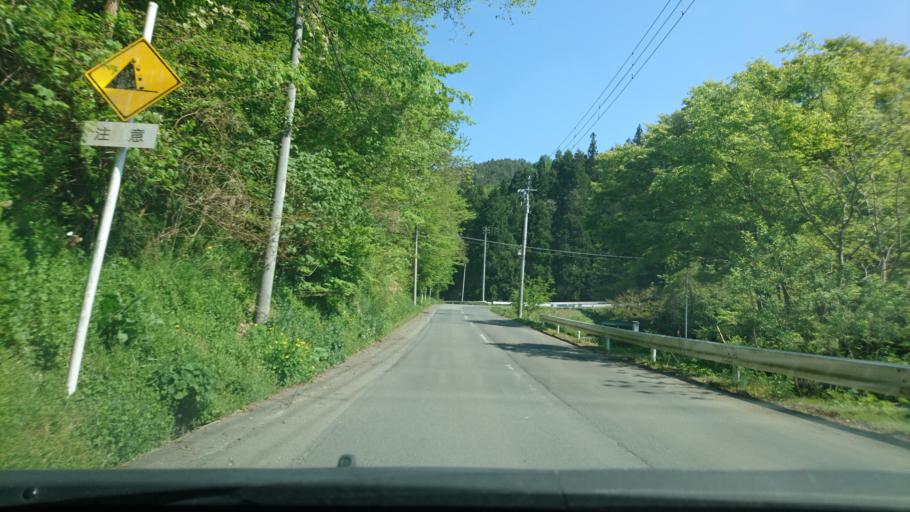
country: JP
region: Iwate
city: Ichinoseki
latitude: 38.9326
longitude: 141.2791
